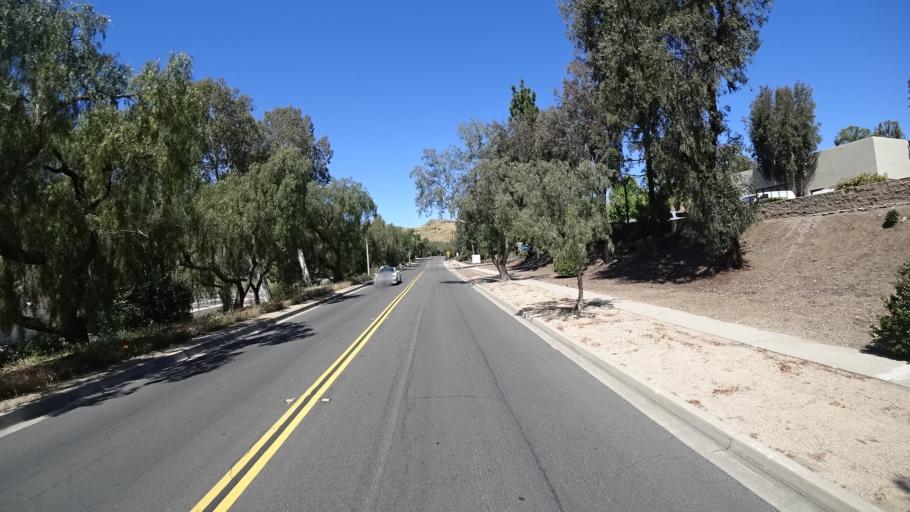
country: US
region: California
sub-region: Ventura County
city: Casa Conejo
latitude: 34.1925
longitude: -118.9558
